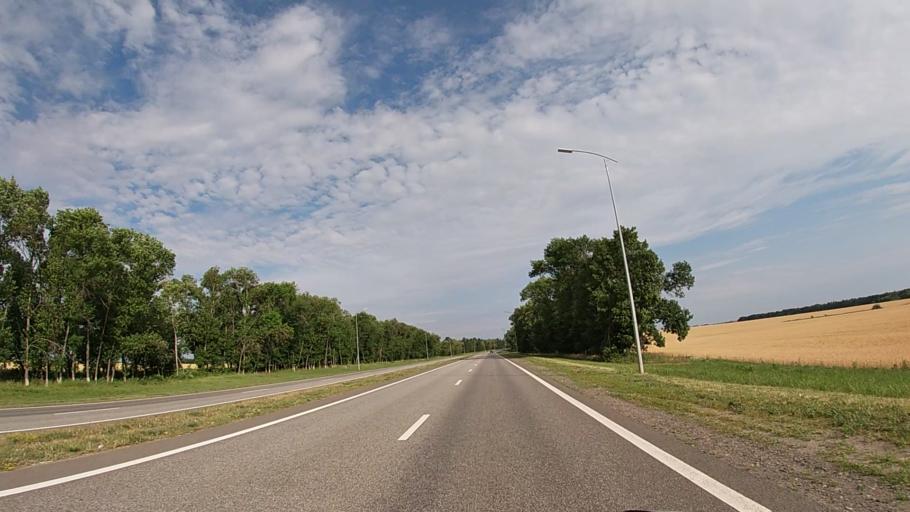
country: RU
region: Belgorod
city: Tomarovka
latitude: 50.6708
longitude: 36.3022
